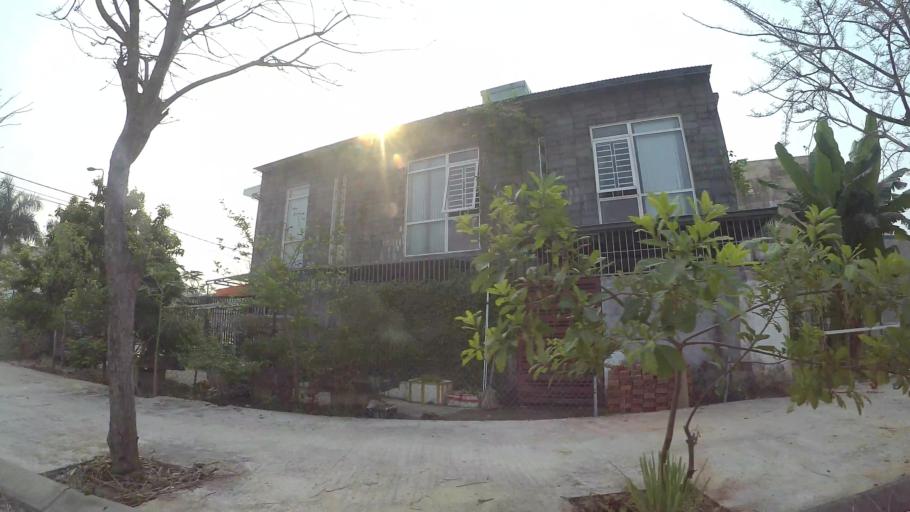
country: VN
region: Da Nang
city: Cam Le
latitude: 16.0146
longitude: 108.2175
